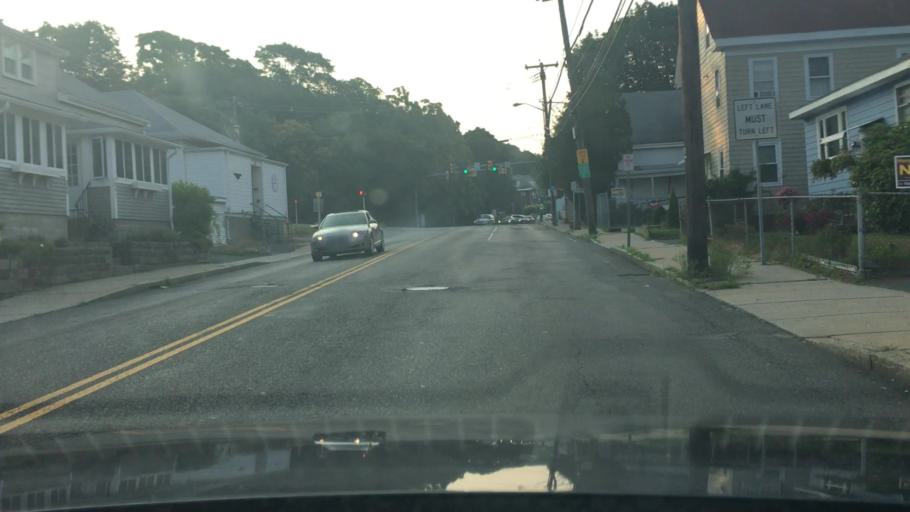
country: US
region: Massachusetts
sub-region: Essex County
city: Lynn
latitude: 42.4711
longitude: -70.9789
